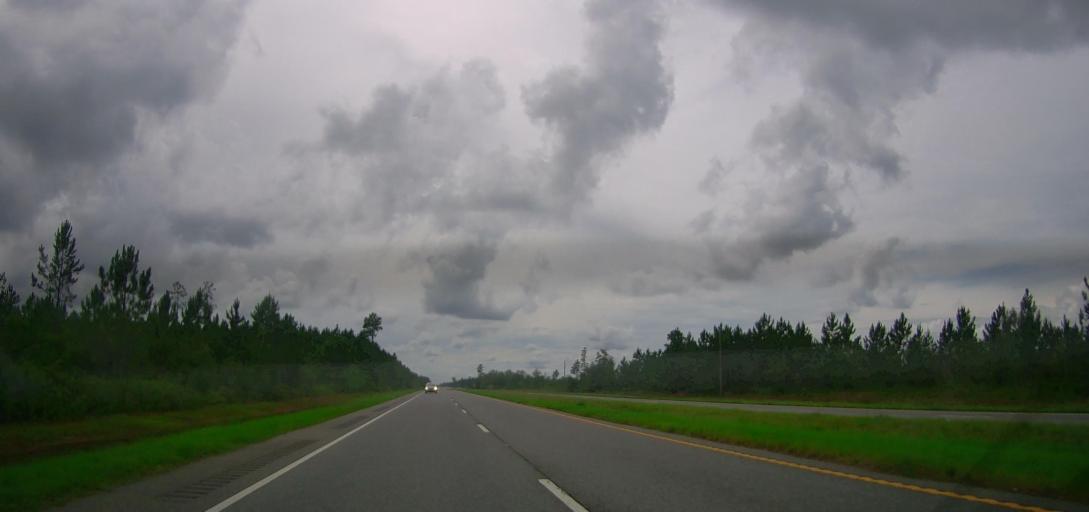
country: US
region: Georgia
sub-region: Wayne County
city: Jesup
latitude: 31.6731
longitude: -82.0653
